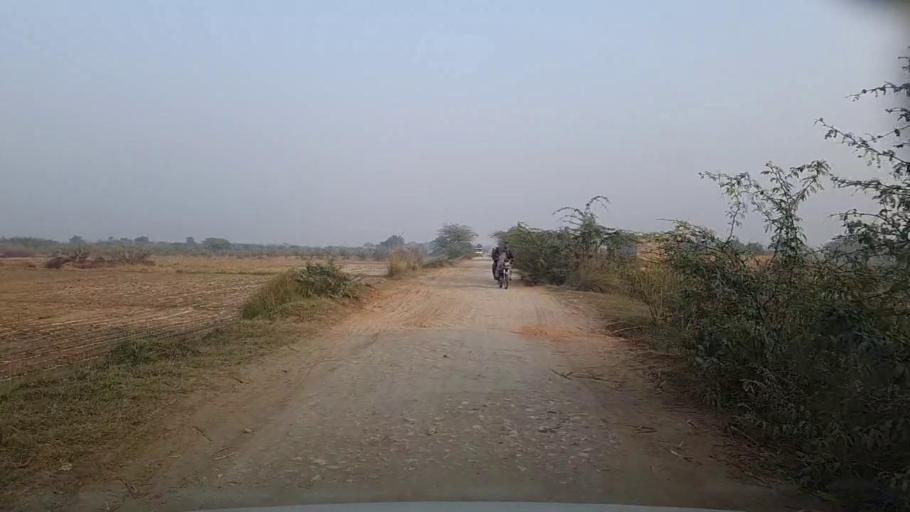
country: PK
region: Sindh
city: Bozdar
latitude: 27.0751
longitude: 68.5864
